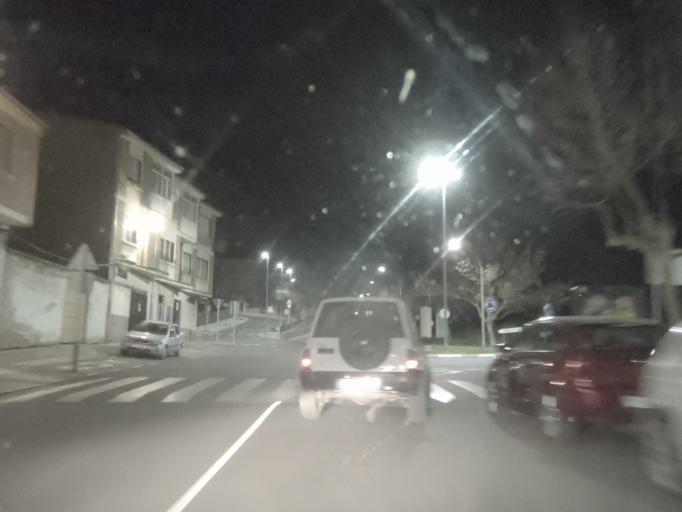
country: ES
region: Castille and Leon
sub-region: Provincia de Zamora
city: Benavente
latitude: 42.0073
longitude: -5.6844
